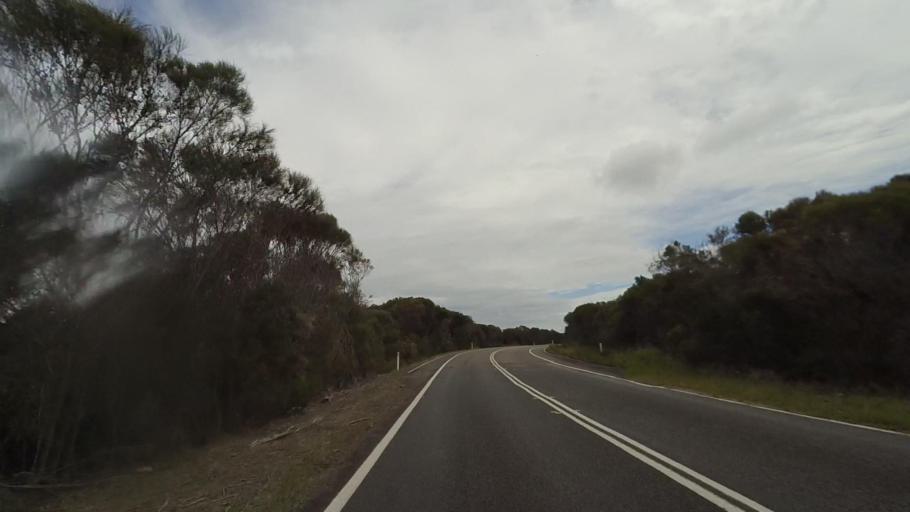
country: AU
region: New South Wales
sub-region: Sutherland Shire
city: Bundeena
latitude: -34.1010
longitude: 151.1220
